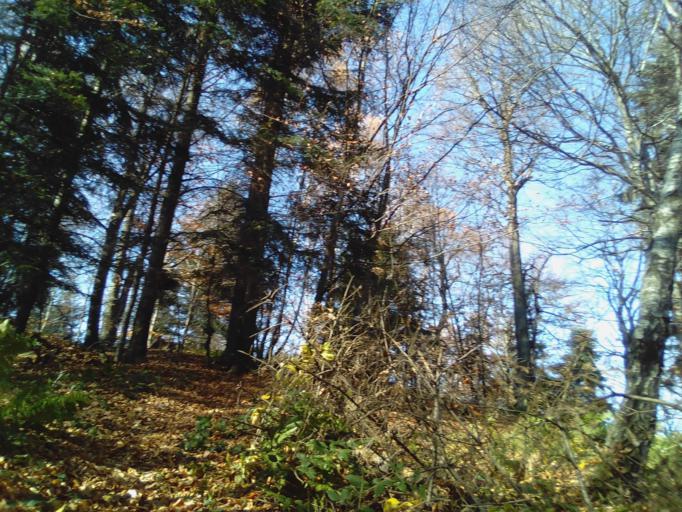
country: PL
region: Subcarpathian Voivodeship
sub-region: Powiat krosnienski
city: Leki
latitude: 49.8206
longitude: 21.6988
